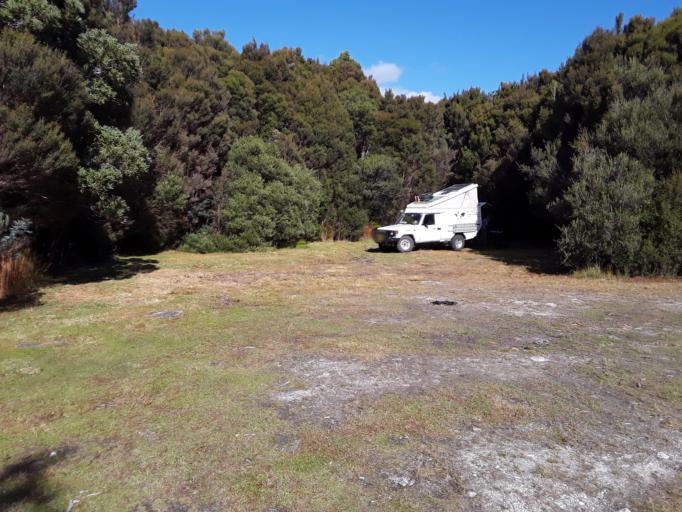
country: AU
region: Tasmania
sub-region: West Coast
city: Queenstown
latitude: -42.0953
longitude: 145.6756
